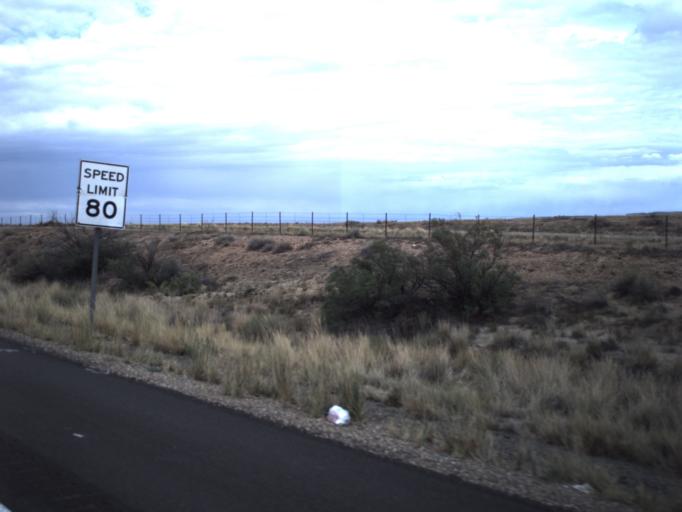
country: US
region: Colorado
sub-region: Mesa County
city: Loma
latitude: 39.0441
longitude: -109.2744
